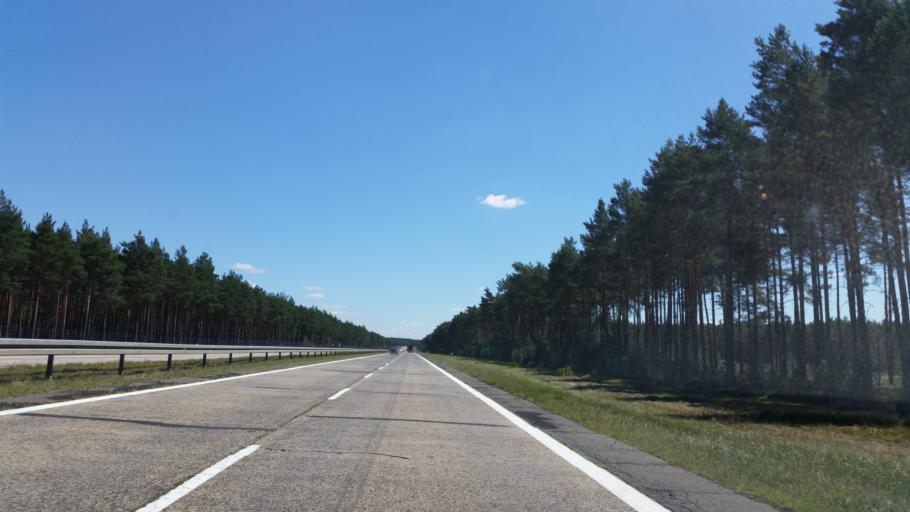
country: PL
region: Lubusz
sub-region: Powiat zaganski
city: Malomice
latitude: 51.4241
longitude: 15.4475
